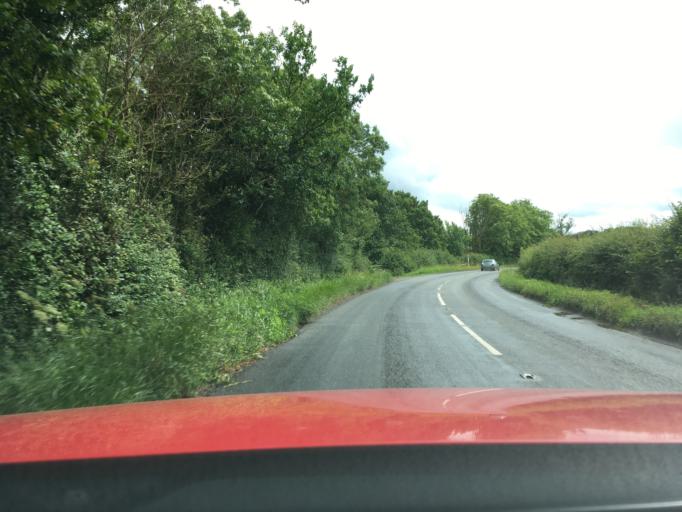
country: GB
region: England
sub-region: Worcestershire
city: Evesham
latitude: 52.0305
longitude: -1.9607
